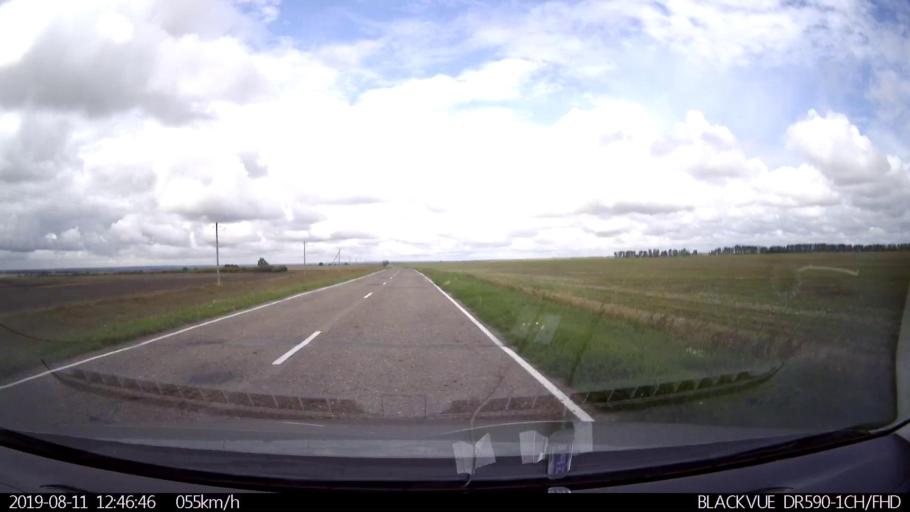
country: RU
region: Ulyanovsk
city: Ignatovka
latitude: 53.8660
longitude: 47.7154
